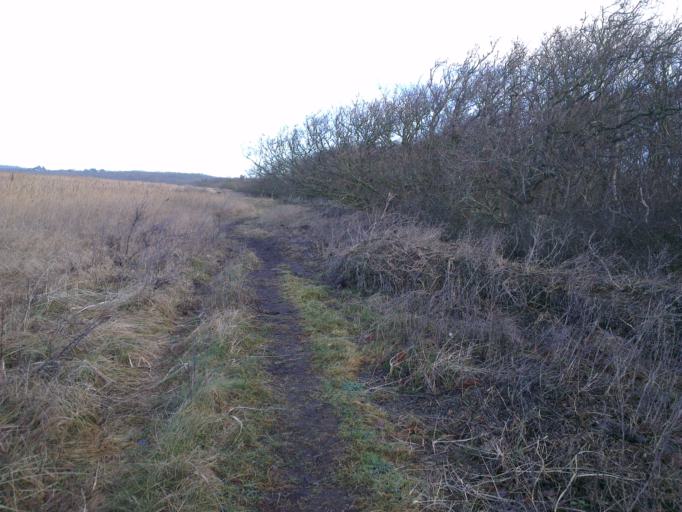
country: DK
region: Capital Region
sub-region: Frederikssund Kommune
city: Jaegerspris
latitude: 55.8440
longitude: 11.9588
